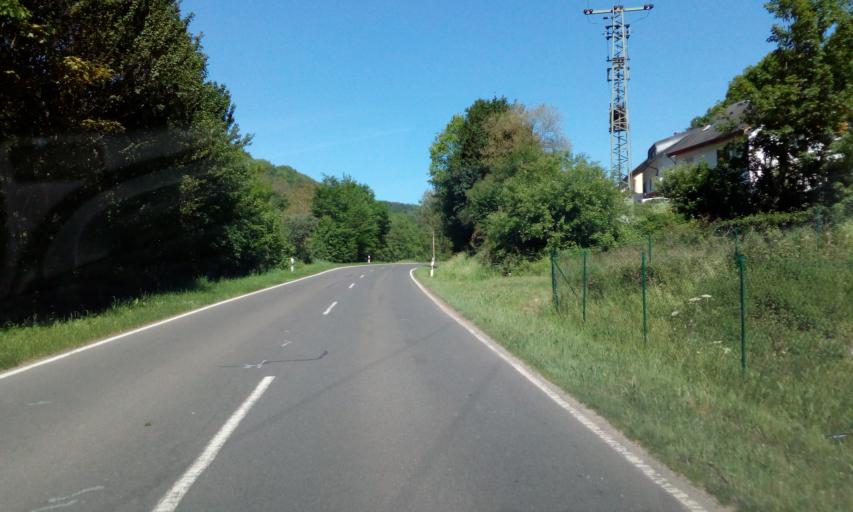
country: DE
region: Rheinland-Pfalz
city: Heidenburg
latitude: 49.8276
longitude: 6.9378
